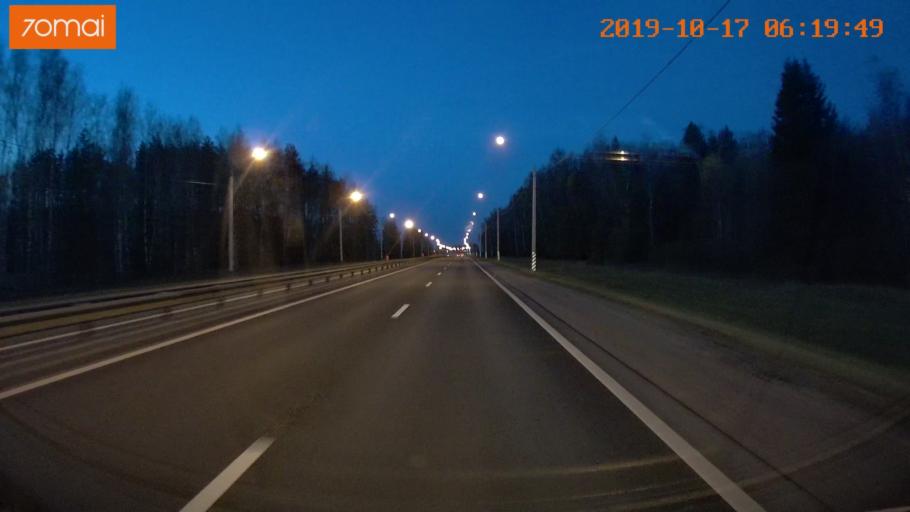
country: RU
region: Ivanovo
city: Lezhnevo
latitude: 56.8236
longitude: 40.8949
